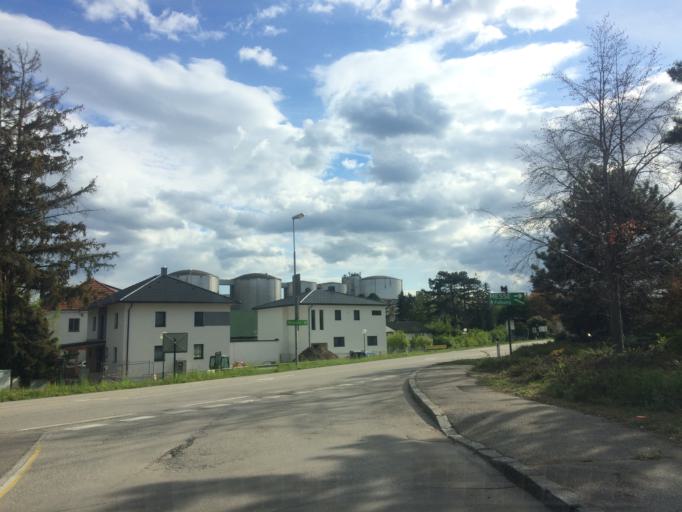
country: AT
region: Lower Austria
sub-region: Politischer Bezirk Tulln
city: Tulln
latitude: 48.3281
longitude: 16.0437
